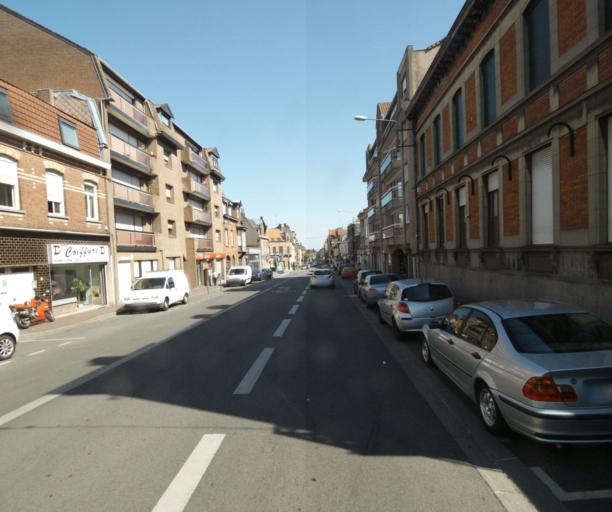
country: FR
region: Nord-Pas-de-Calais
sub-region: Departement du Nord
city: Halluin
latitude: 50.7820
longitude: 3.1259
